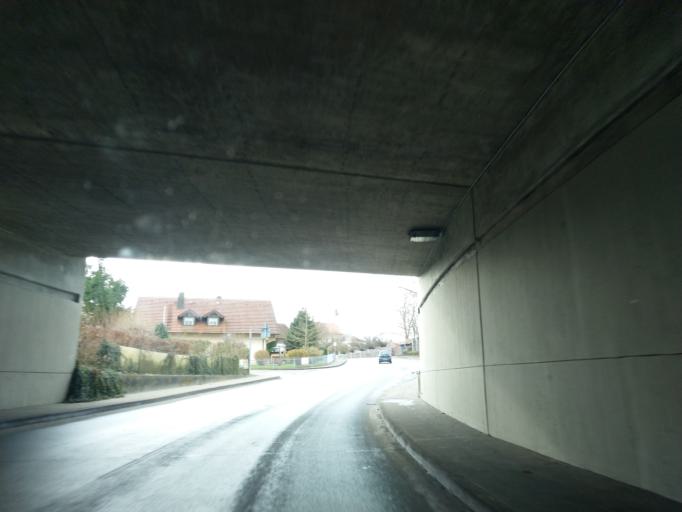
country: DE
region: Bavaria
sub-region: Lower Bavaria
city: Osterhofen
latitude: 48.6949
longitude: 13.0209
